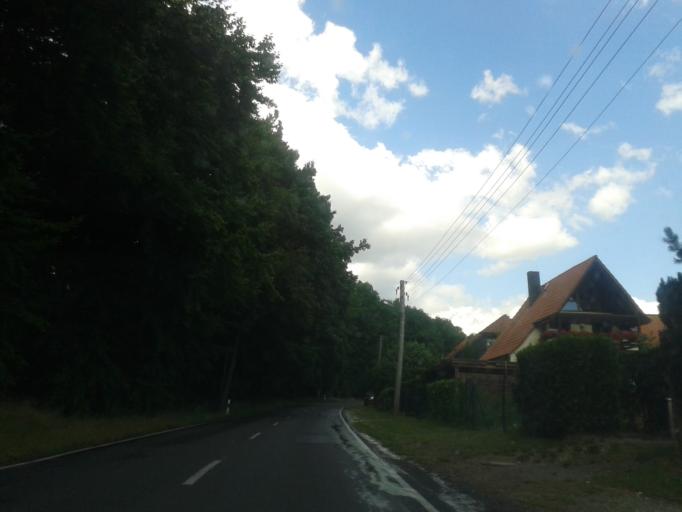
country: DE
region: Saxony
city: Radeberg
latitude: 51.0767
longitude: 13.8891
